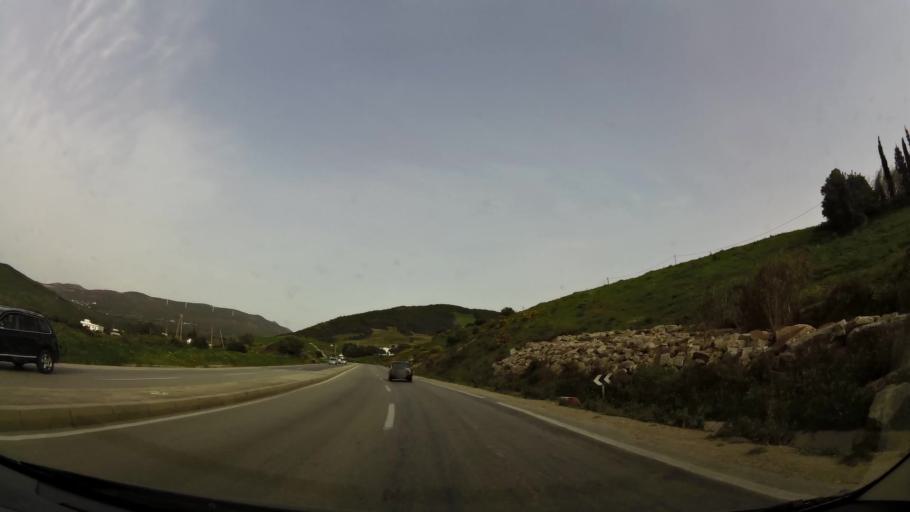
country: MA
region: Tanger-Tetouan
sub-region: Tanger-Assilah
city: Dar Chaoui
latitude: 35.5631
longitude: -5.6007
